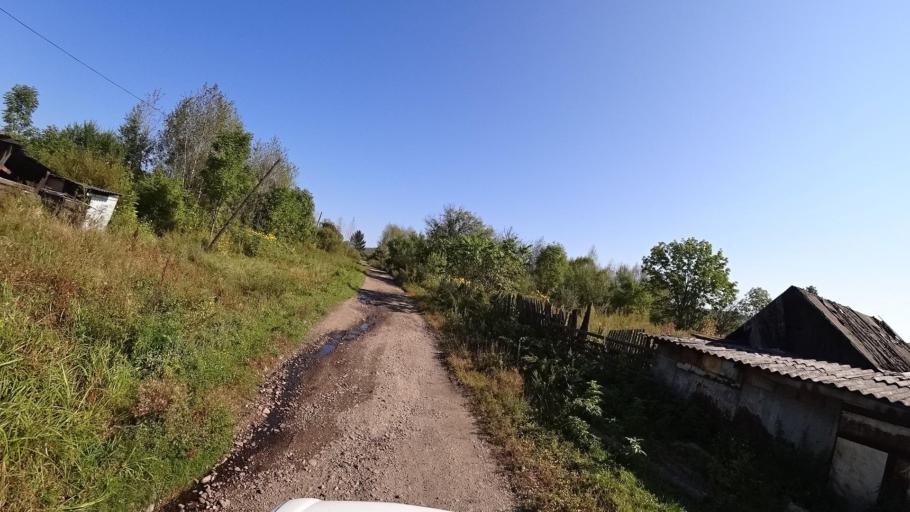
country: RU
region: Jewish Autonomous Oblast
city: Bira
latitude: 49.0009
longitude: 132.4716
